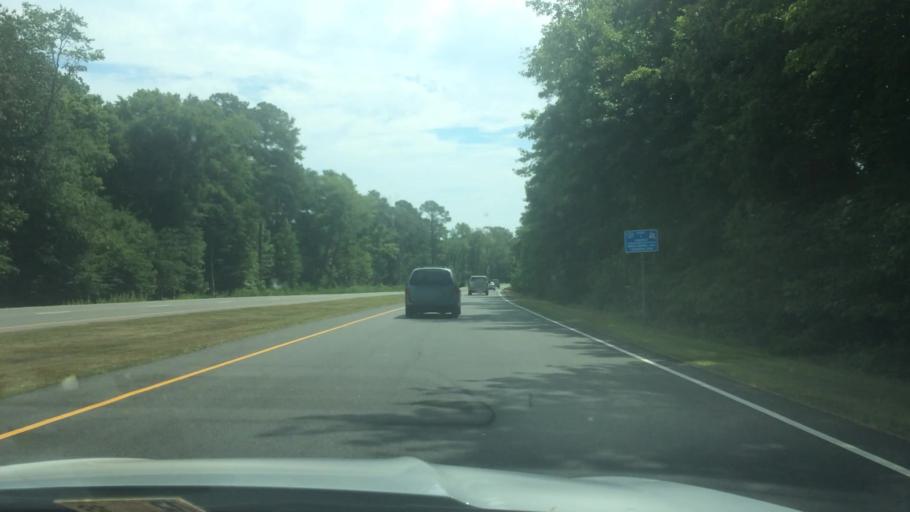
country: US
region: Virginia
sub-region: City of Poquoson
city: Poquoson
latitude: 37.1206
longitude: -76.4463
